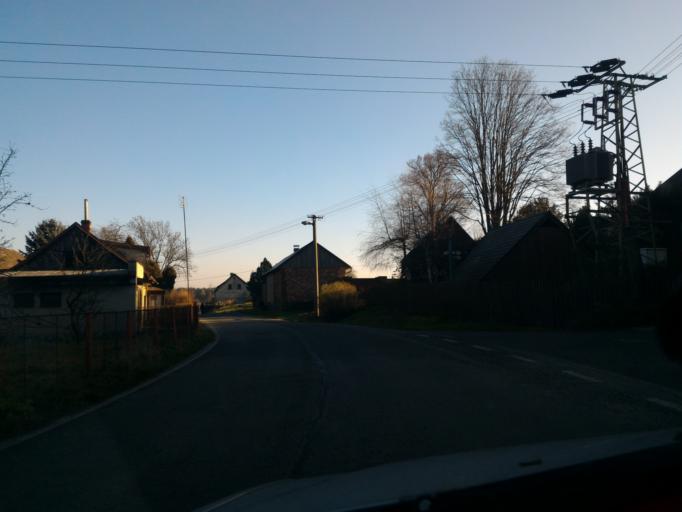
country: CZ
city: Jablonne v Podjestedi
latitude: 50.7948
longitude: 14.7236
